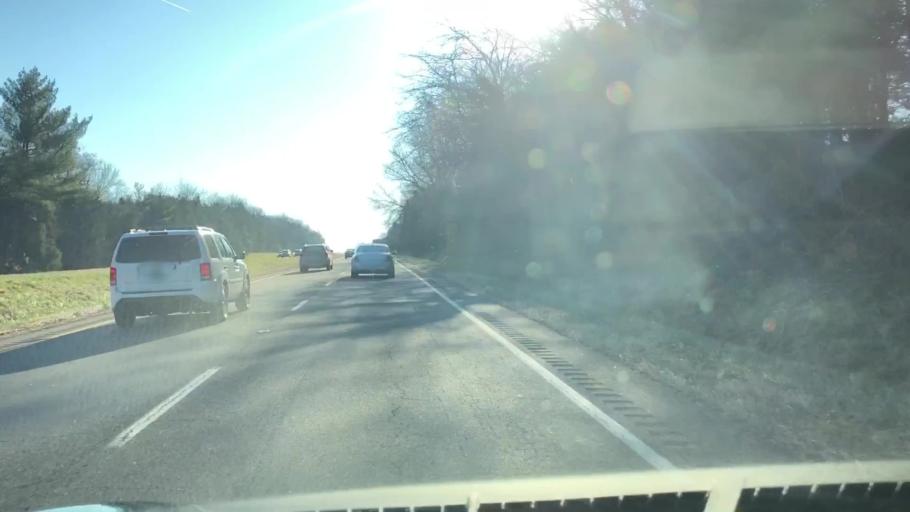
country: US
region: Virginia
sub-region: Fauquier County
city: Bealeton
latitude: 38.5460
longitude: -77.8101
